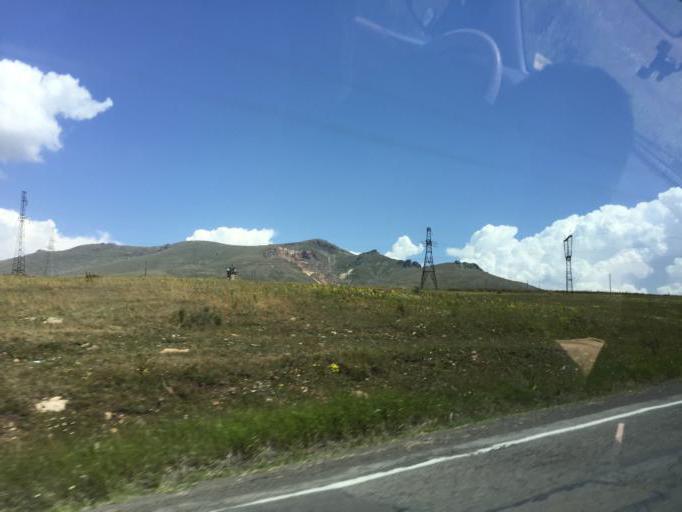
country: AM
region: Vayots' Dzori Marz
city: Jermuk
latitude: 39.6860
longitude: 45.7094
